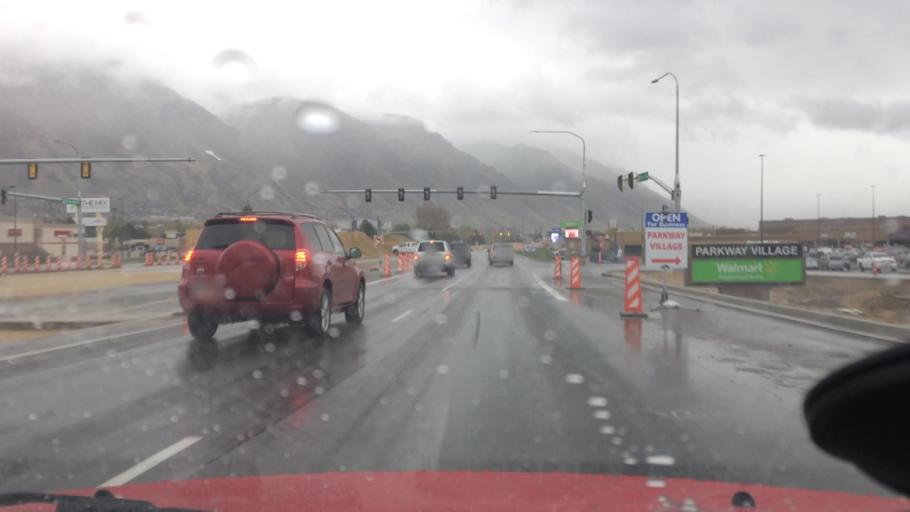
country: US
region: Utah
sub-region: Utah County
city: Provo
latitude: 40.2650
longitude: -111.6707
